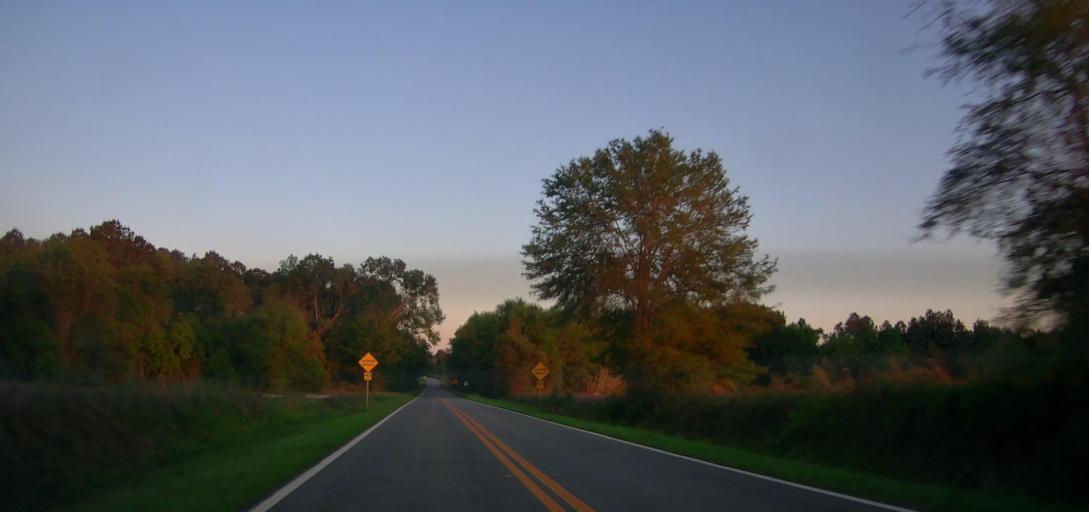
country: US
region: Georgia
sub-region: Wilcox County
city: Rochelle
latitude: 31.8033
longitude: -83.4550
